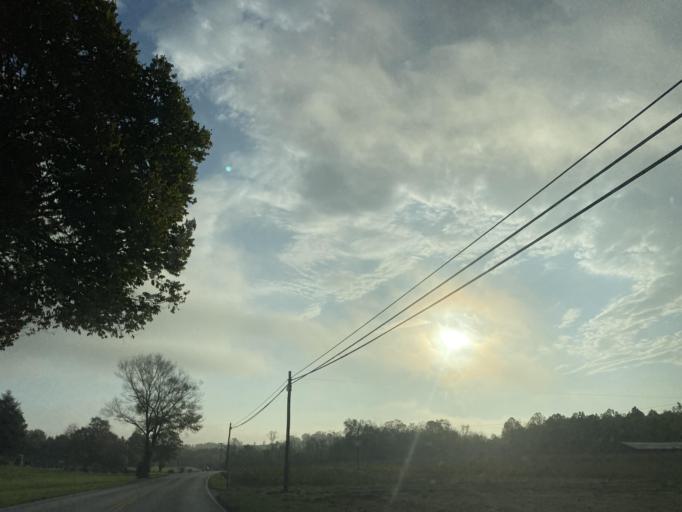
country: US
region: Kentucky
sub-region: Pendleton County
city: Falmouth
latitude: 38.7927
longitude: -84.3509
